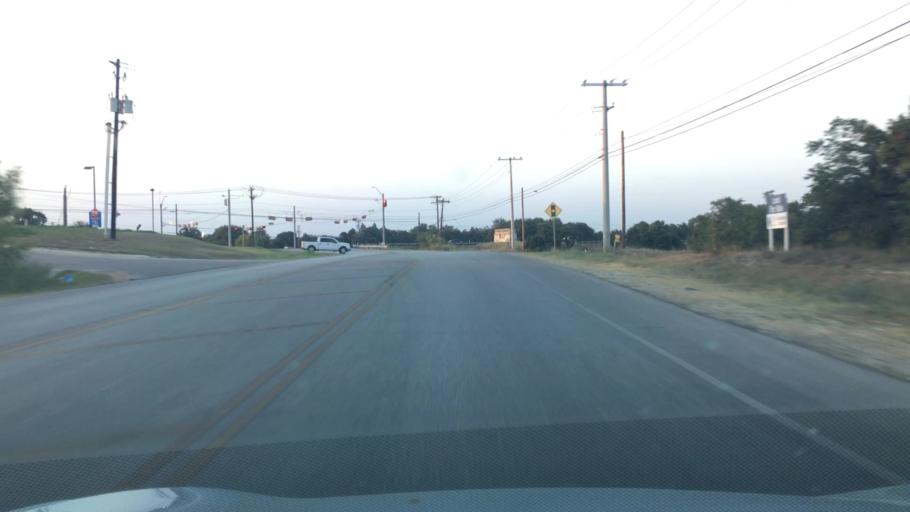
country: US
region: Texas
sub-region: Hays County
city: Dripping Springs
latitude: 30.1952
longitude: -97.9977
